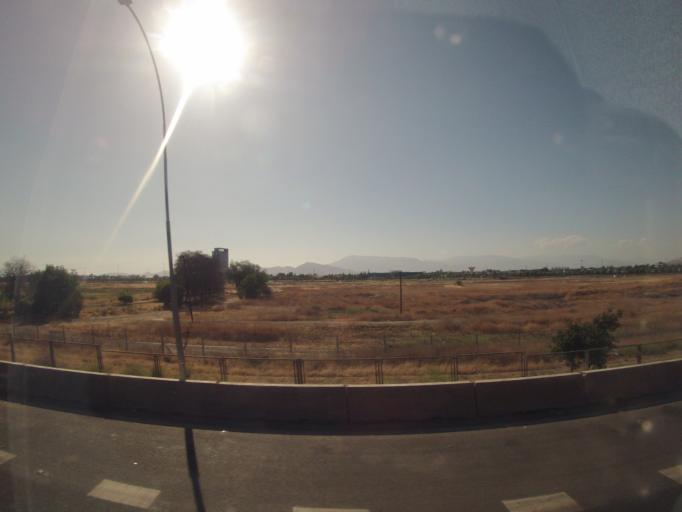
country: CL
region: Santiago Metropolitan
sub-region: Provincia de Santiago
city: Santiago
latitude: -33.4900
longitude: -70.6898
